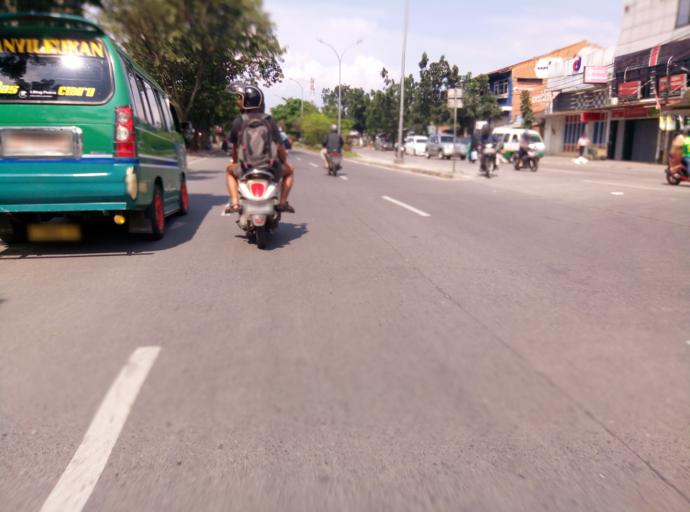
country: ID
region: West Java
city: Bandung
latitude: -6.9346
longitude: 107.6427
